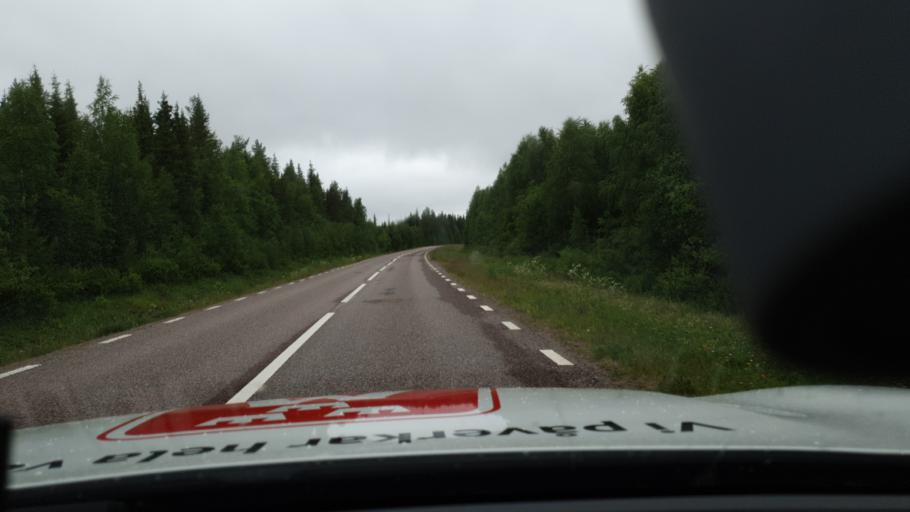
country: FI
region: Lapland
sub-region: Torniolaakso
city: Pello
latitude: 66.9199
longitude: 23.8544
